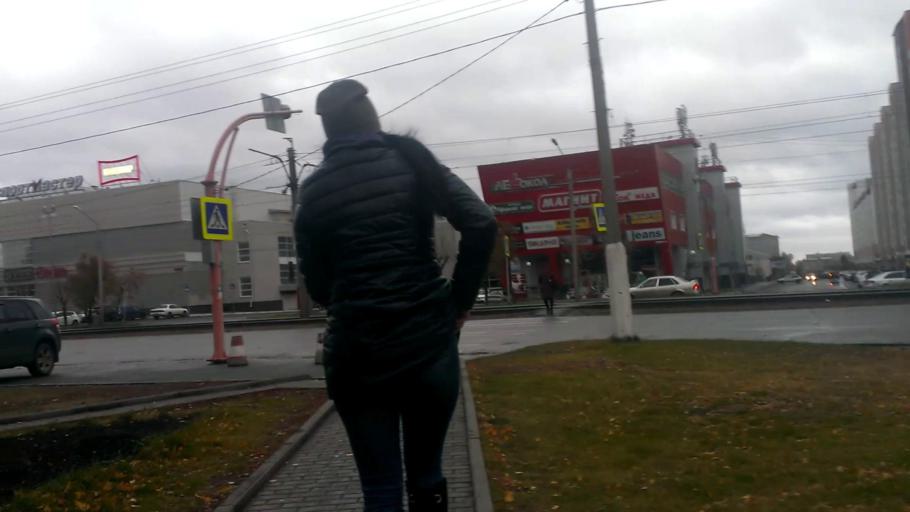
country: RU
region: Altai Krai
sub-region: Gorod Barnaulskiy
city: Barnaul
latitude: 53.3603
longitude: 83.6962
